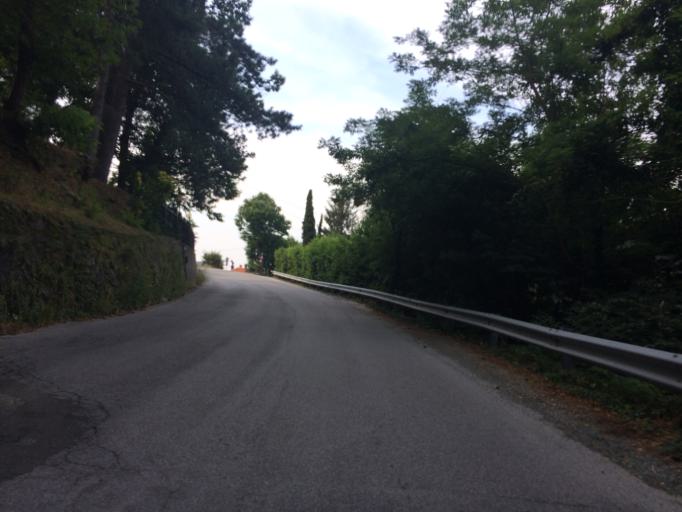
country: IT
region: Liguria
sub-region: Provincia di Savona
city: San Giovanni
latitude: 44.4005
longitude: 8.4938
